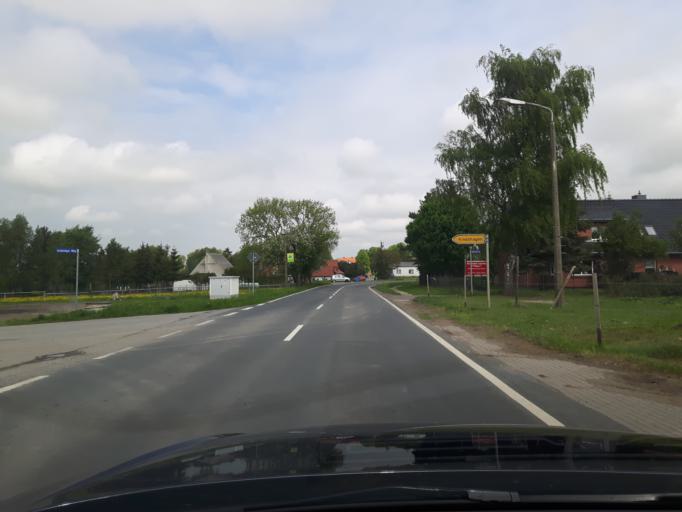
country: DE
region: Mecklenburg-Vorpommern
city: Barth
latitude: 54.2903
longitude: 12.7178
